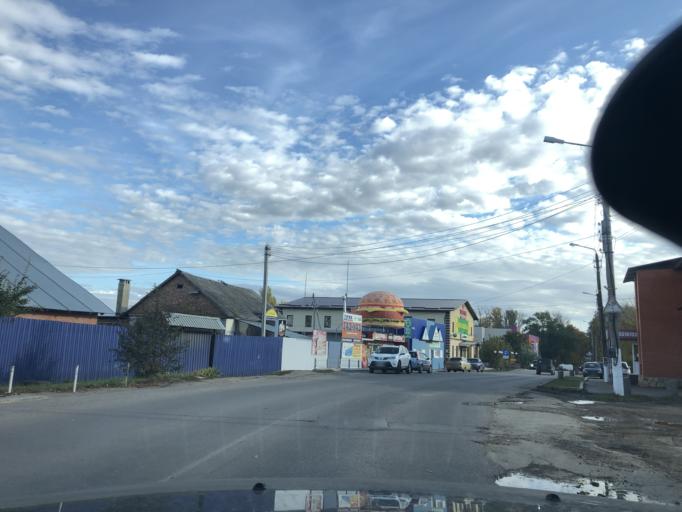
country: RU
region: Tula
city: Kireyevsk
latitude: 53.9314
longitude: 37.9269
